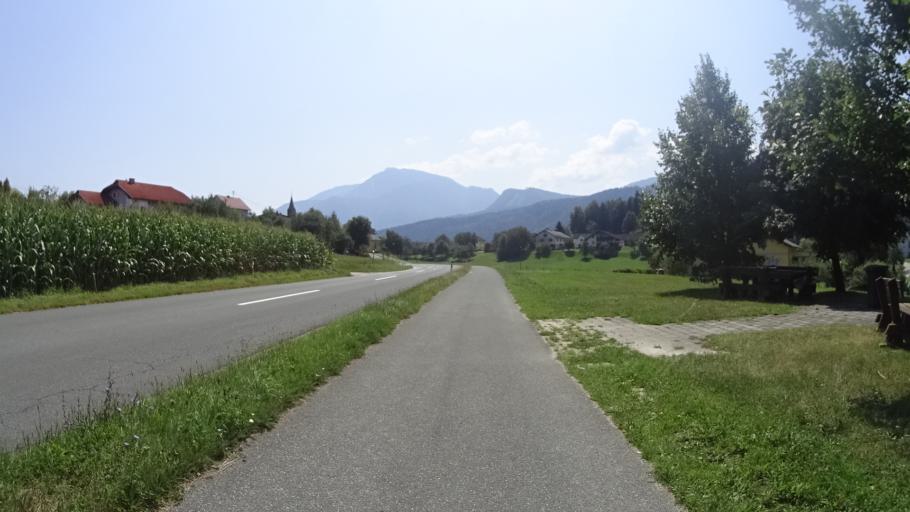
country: AT
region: Carinthia
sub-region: Politischer Bezirk Volkermarkt
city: Eberndorf
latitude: 46.5700
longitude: 14.6631
